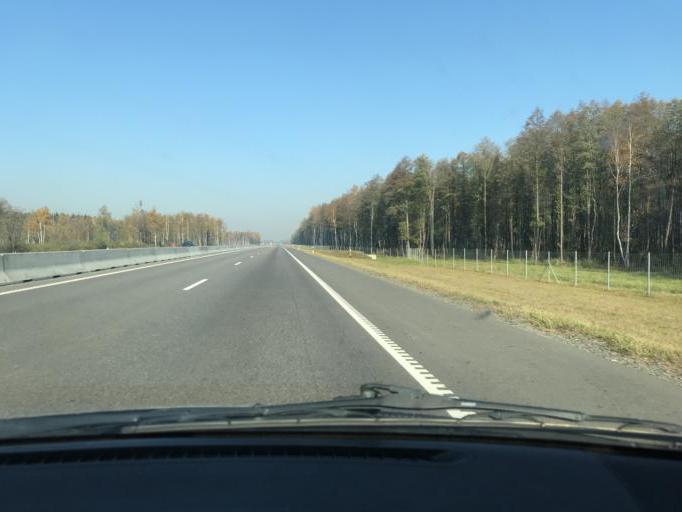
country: BY
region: Minsk
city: Slutsk
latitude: 53.2497
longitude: 27.5504
